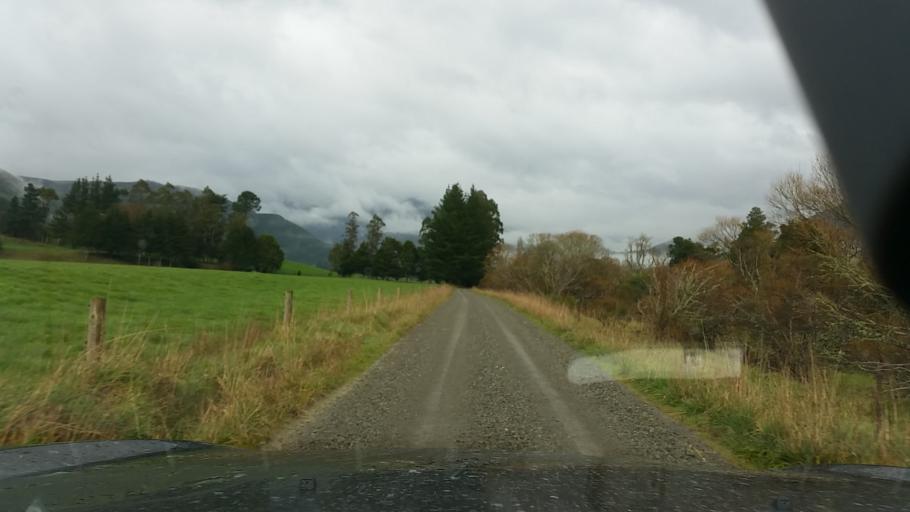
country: NZ
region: Nelson
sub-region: Nelson City
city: Nelson
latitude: -41.2613
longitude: 173.5766
